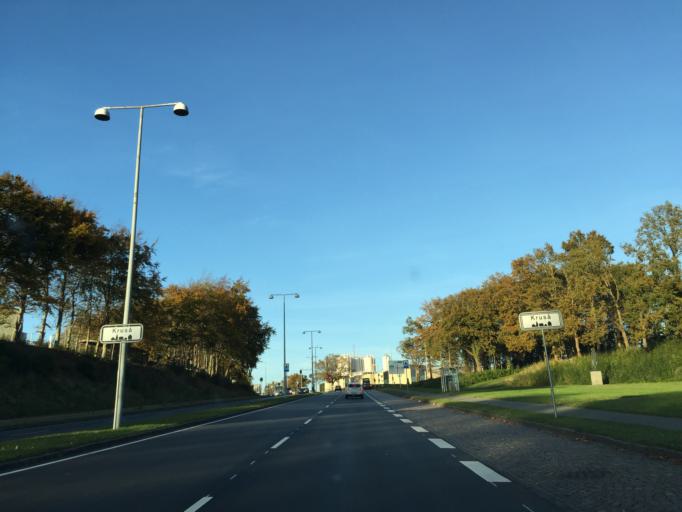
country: DK
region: South Denmark
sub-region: Aabenraa Kommune
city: Krusa
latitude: 54.8478
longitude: 9.4013
